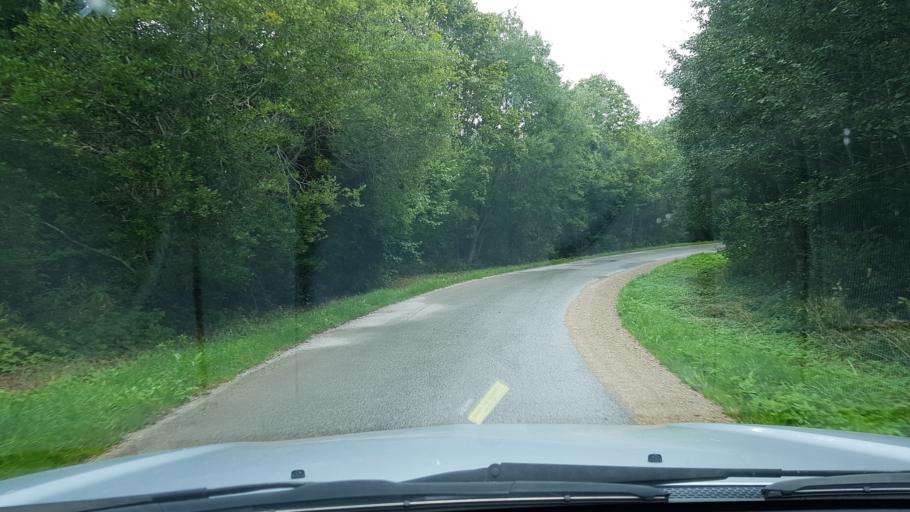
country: EE
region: Harju
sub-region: Rae vald
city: Jueri
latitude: 59.3736
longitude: 24.9352
